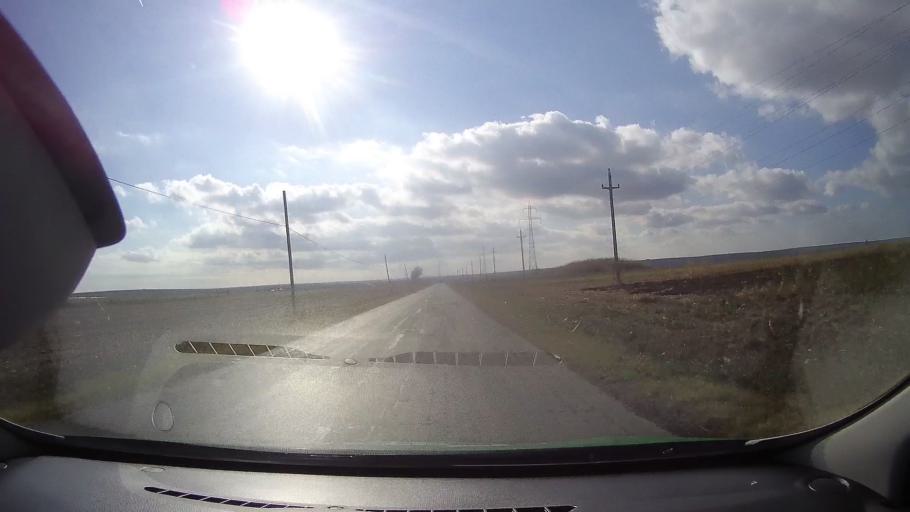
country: RO
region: Constanta
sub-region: Comuna Istria
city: Nuntasi
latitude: 44.5372
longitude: 28.6875
